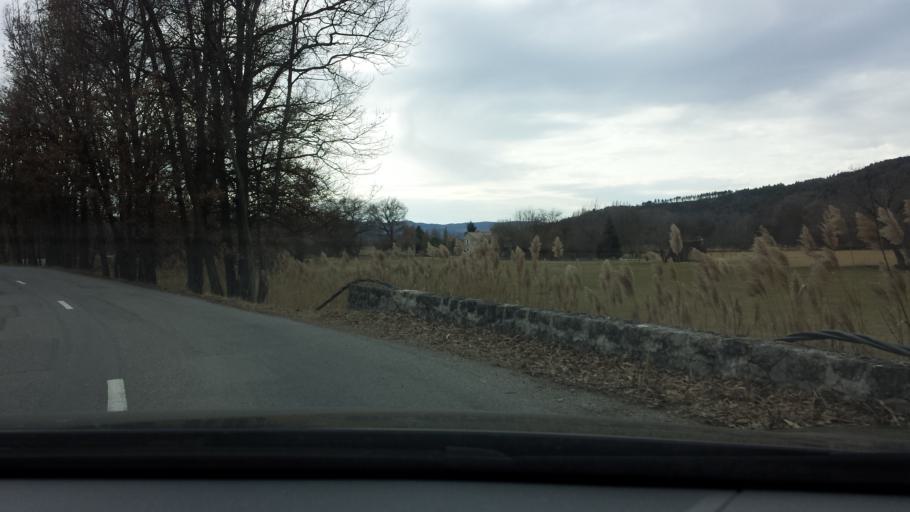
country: FR
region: Provence-Alpes-Cote d'Azur
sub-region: Departement des Alpes-de-Haute-Provence
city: Mallemoisson
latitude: 44.0624
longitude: 6.1794
